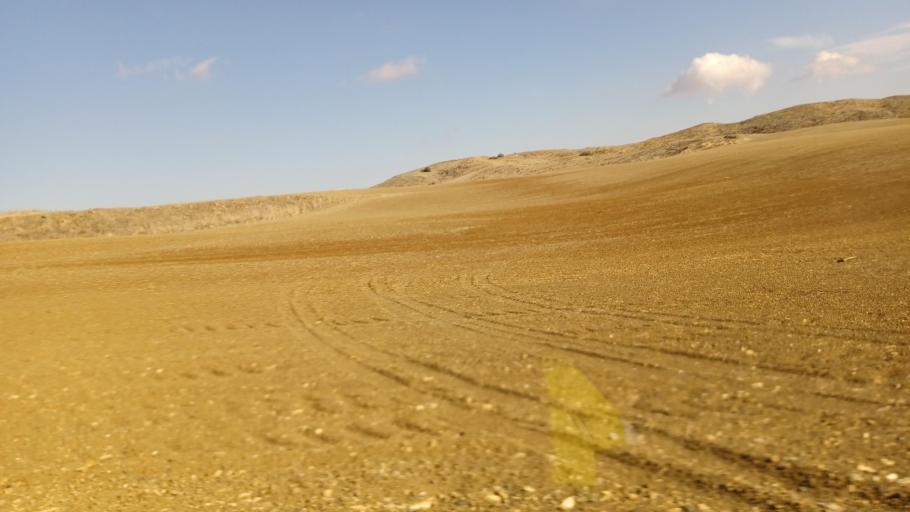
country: CY
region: Larnaka
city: Troulloi
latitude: 35.0206
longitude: 33.5851
